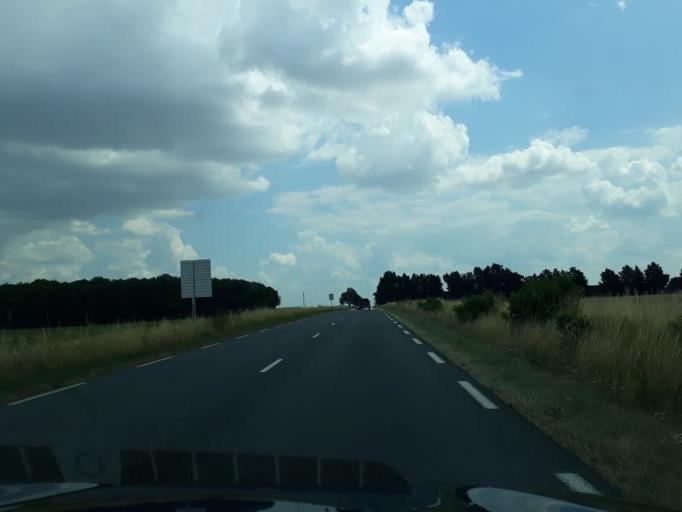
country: FR
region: Centre
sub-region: Departement du Cher
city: Avord
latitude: 47.0342
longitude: 2.6263
